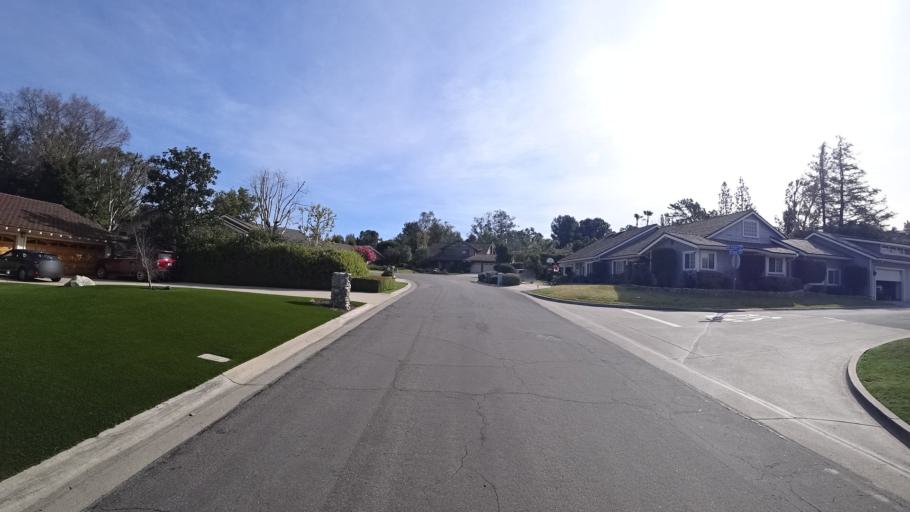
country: US
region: California
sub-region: Orange County
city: Yorba Linda
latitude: 33.8590
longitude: -117.7659
